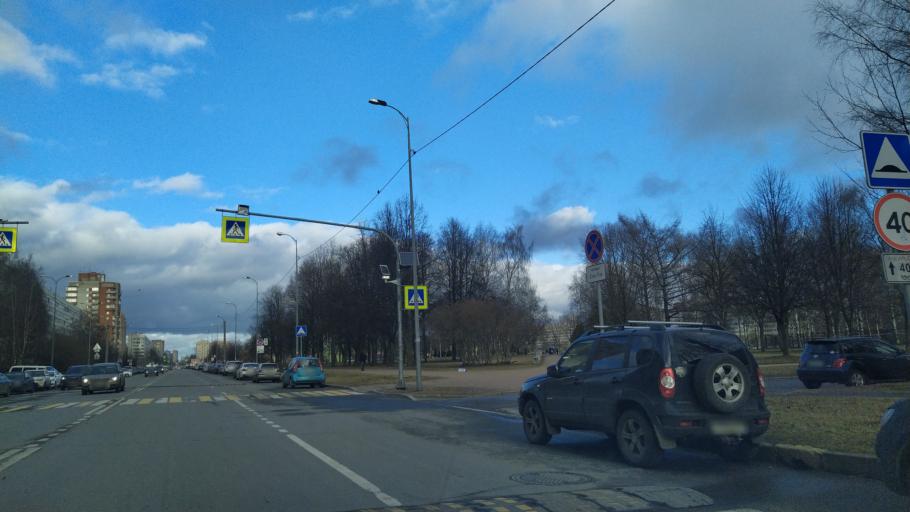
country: RU
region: St.-Petersburg
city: Grazhdanka
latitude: 60.0381
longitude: 30.3830
